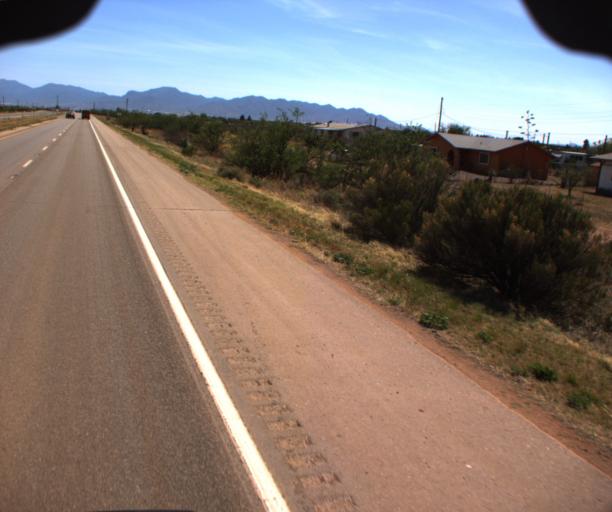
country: US
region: Arizona
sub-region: Cochise County
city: Huachuca City
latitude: 31.7044
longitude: -110.3505
